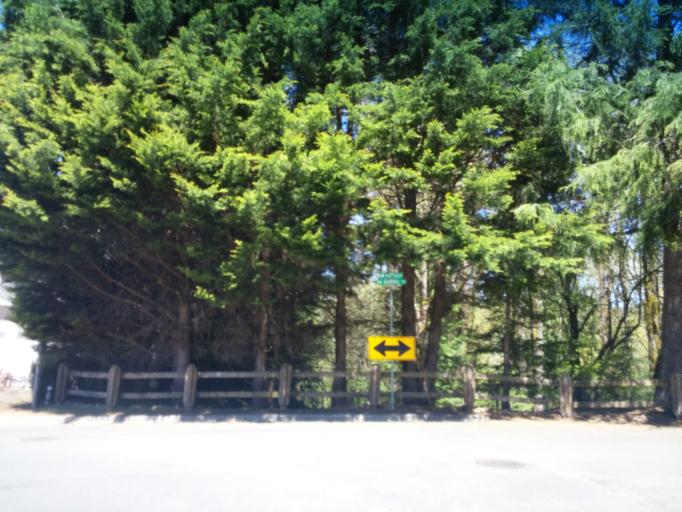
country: US
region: Oregon
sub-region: Washington County
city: West Haven
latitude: 45.5296
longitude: -122.7747
